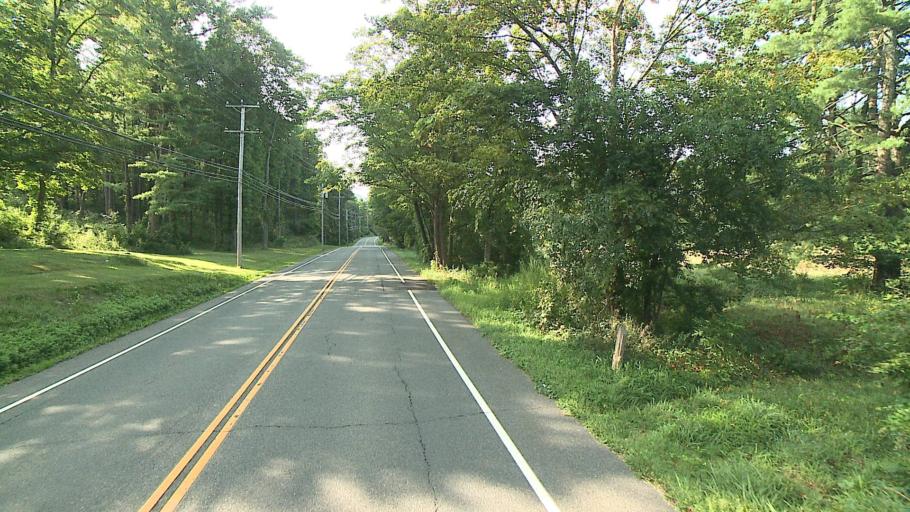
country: US
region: Connecticut
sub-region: Litchfield County
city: Canaan
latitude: 42.0165
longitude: -73.3325
